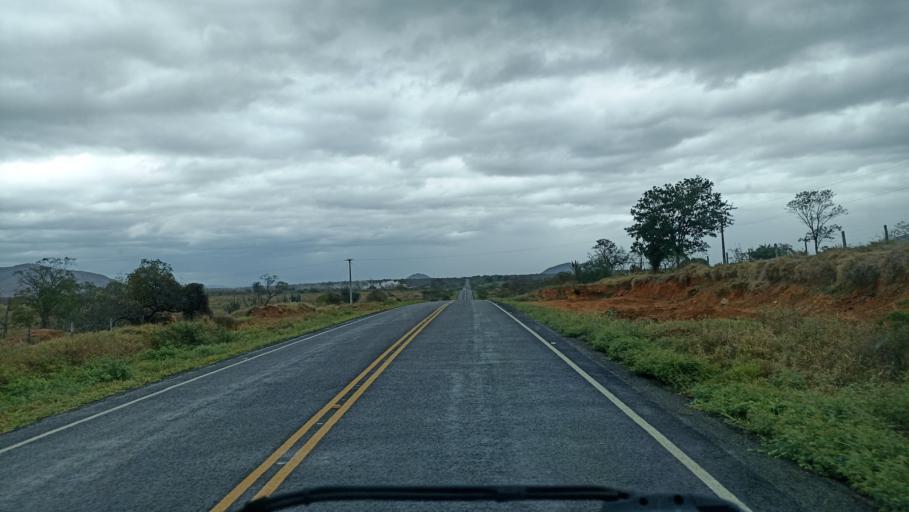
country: BR
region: Bahia
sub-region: Iacu
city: Iacu
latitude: -12.9671
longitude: -40.4924
